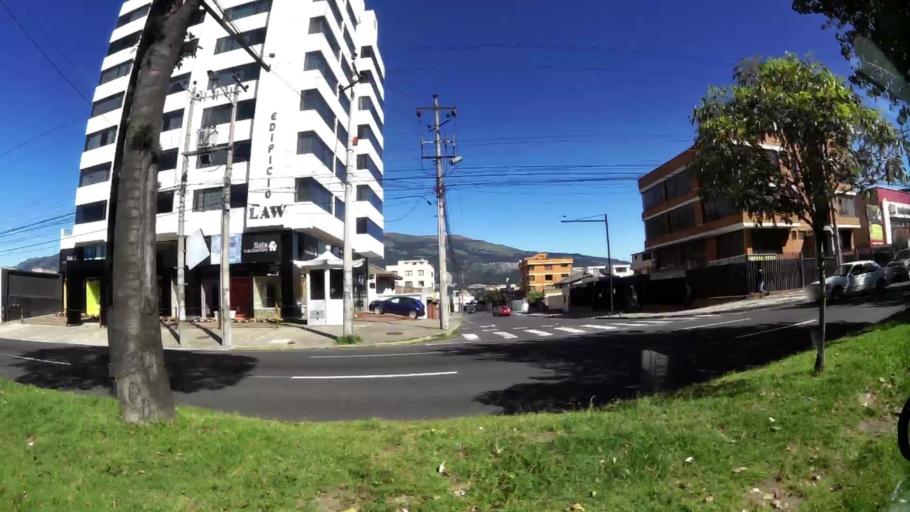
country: EC
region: Pichincha
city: Quito
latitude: -0.1435
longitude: -78.4746
